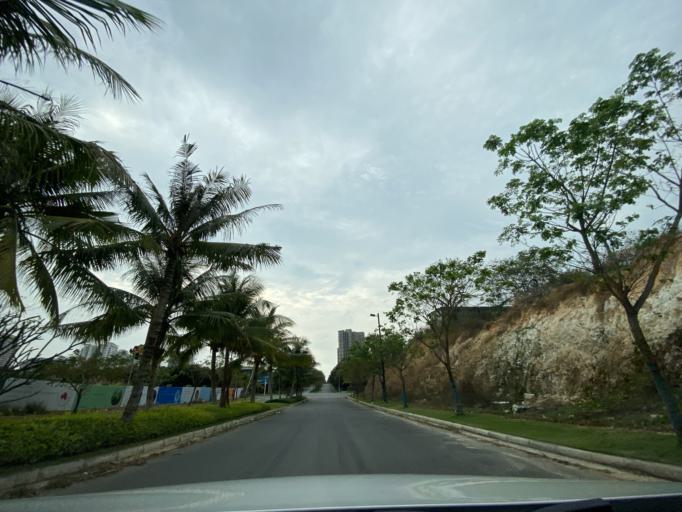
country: CN
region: Hainan
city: Yingzhou
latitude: 18.4190
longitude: 109.8882
